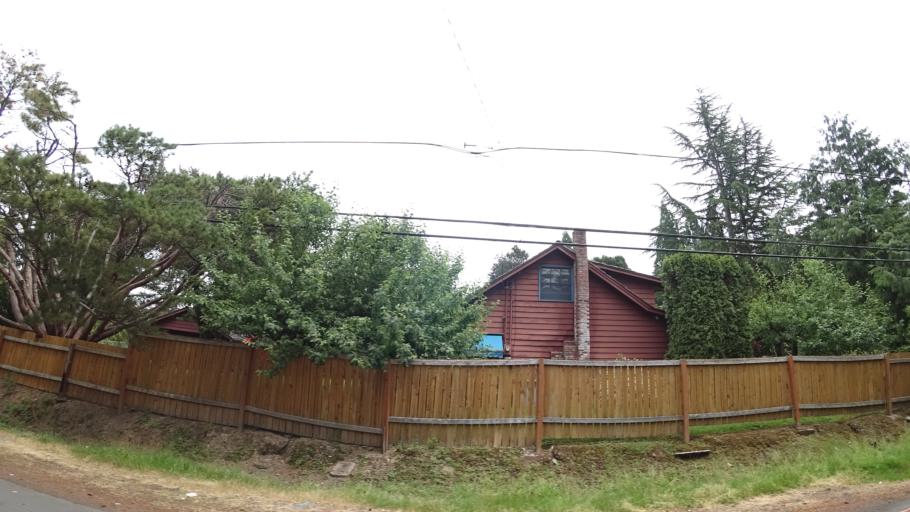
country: US
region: Oregon
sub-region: Washington County
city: Garden Home-Whitford
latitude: 45.4652
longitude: -122.7659
